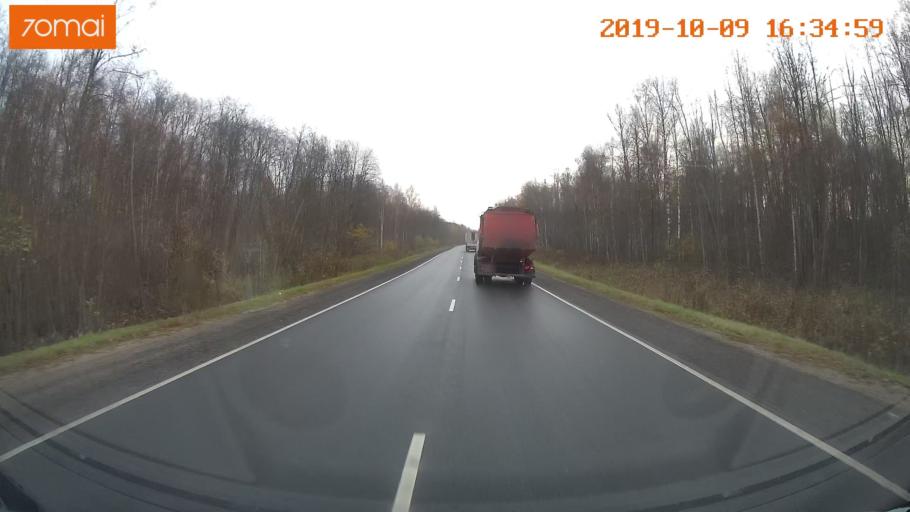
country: RU
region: Kostroma
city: Oktyabr'skiy
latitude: 57.5605
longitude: 40.9967
